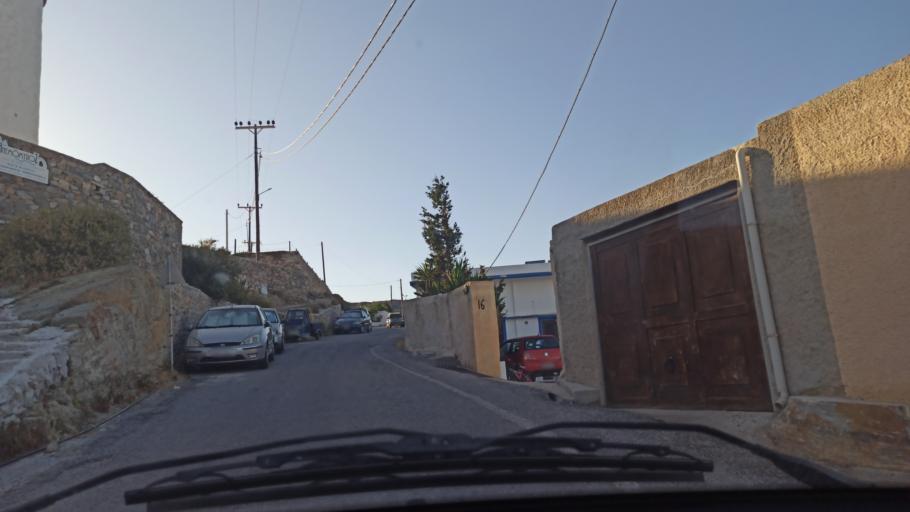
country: GR
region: South Aegean
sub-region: Nomos Kykladon
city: Ano Syros
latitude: 37.4525
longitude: 24.9348
